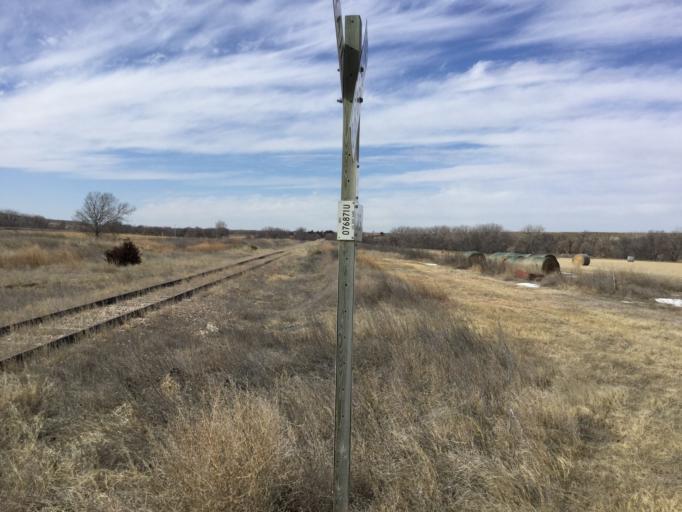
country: US
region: Kansas
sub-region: Rawlins County
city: Atwood
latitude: 39.8221
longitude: -101.1186
